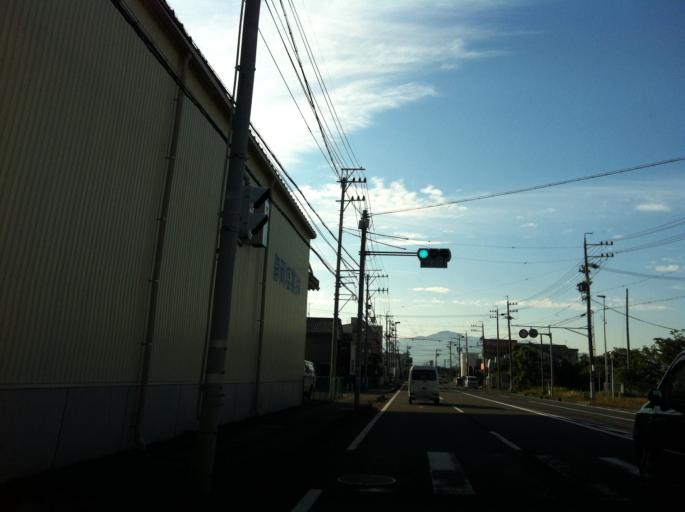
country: JP
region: Shizuoka
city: Shizuoka-shi
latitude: 34.9900
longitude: 138.4968
